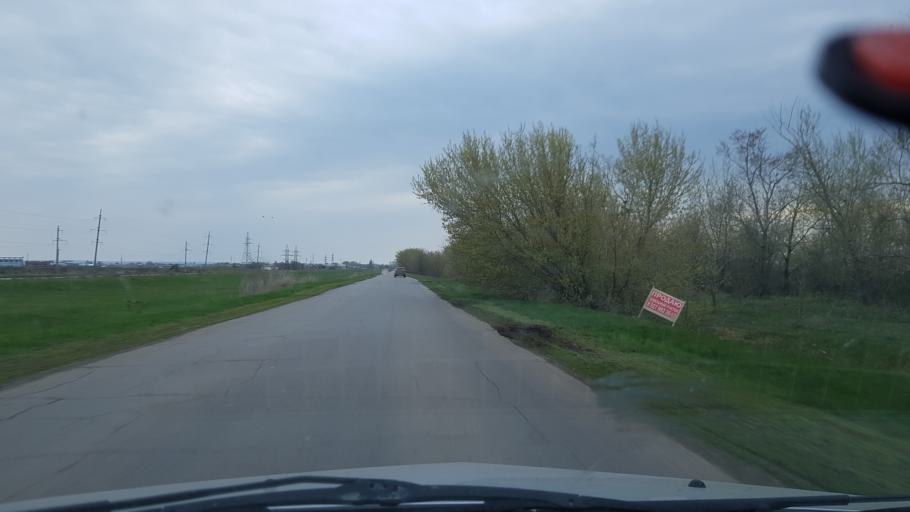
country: RU
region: Samara
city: Khryashchevka
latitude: 53.6712
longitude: 49.1018
